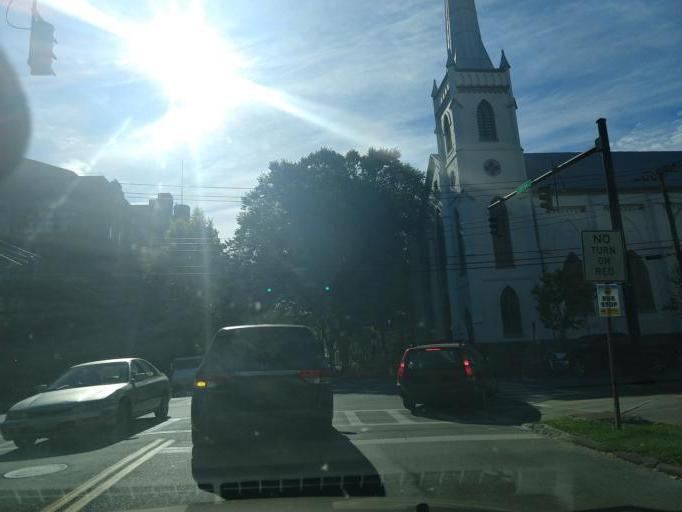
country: US
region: New York
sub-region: Tompkins County
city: Ithaca
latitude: 42.4415
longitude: -76.4991
